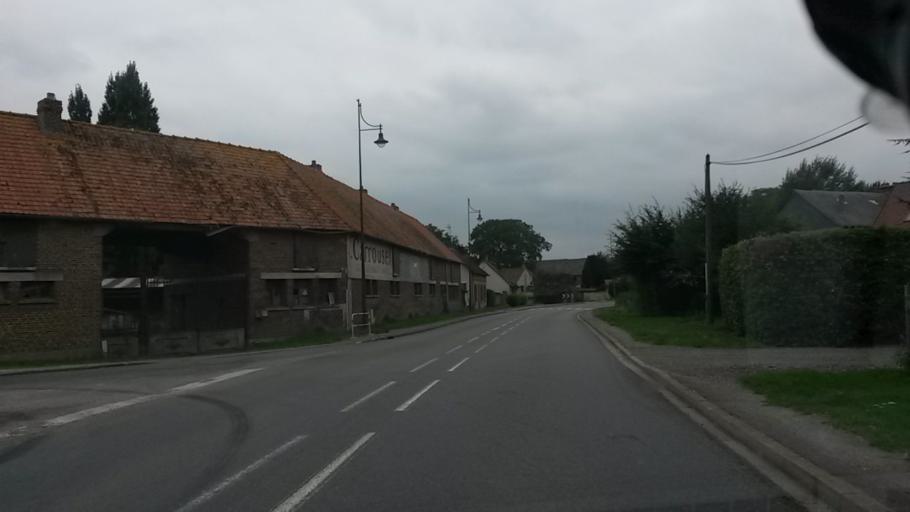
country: FR
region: Picardie
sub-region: Departement de la Somme
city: Hornoy-le-Bourg
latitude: 49.7751
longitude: 1.8688
